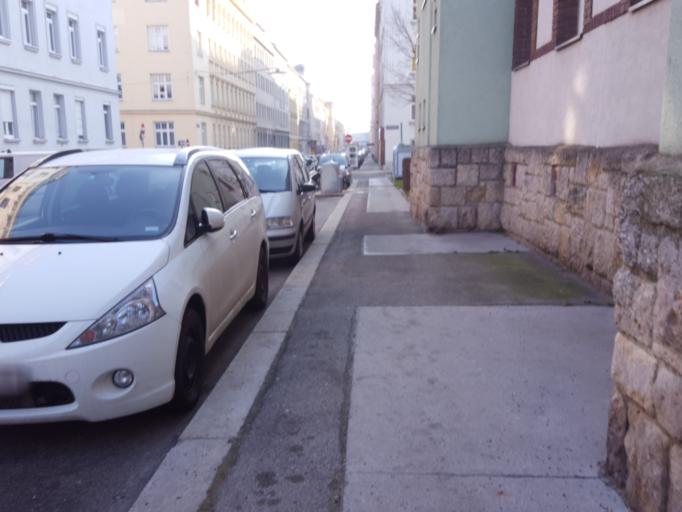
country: AT
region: Vienna
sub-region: Wien Stadt
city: Vienna
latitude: 48.1777
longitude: 16.3216
